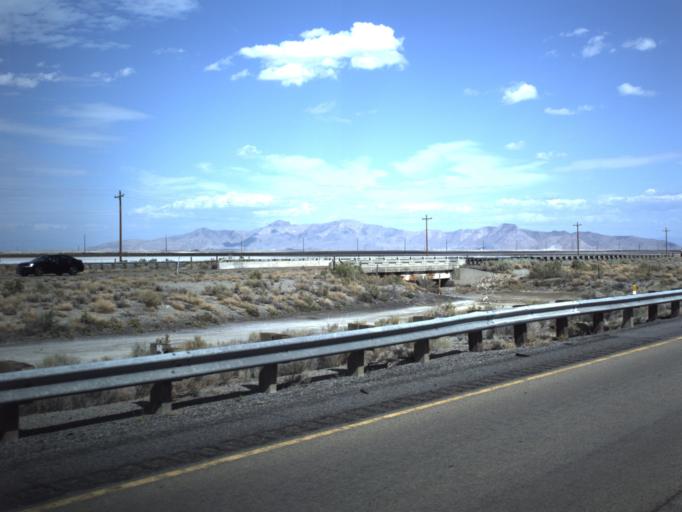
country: US
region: Utah
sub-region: Tooele County
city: Grantsville
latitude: 40.7526
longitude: -112.7230
